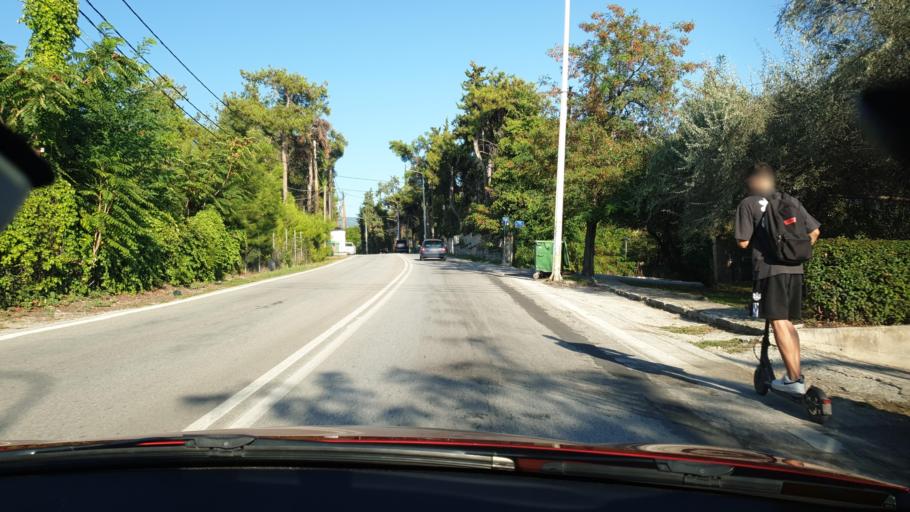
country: GR
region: Central Macedonia
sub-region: Nomos Thessalonikis
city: Panorama
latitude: 40.5921
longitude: 23.0212
